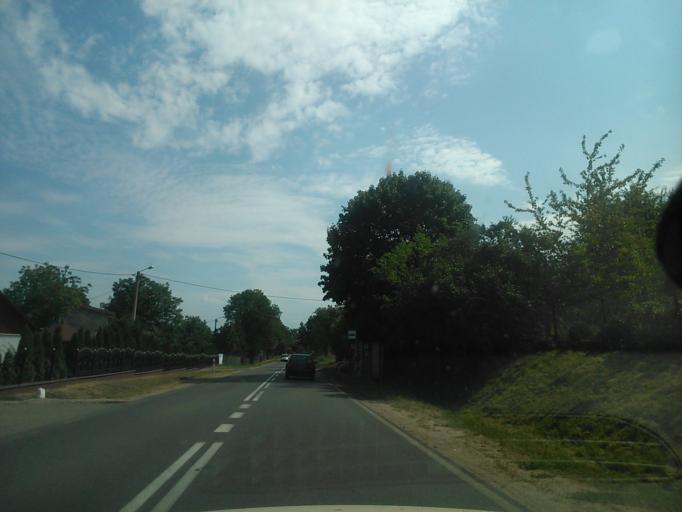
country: PL
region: Warmian-Masurian Voivodeship
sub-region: Powiat dzialdowski
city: Ilowo -Osada
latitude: 53.1538
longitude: 20.3193
